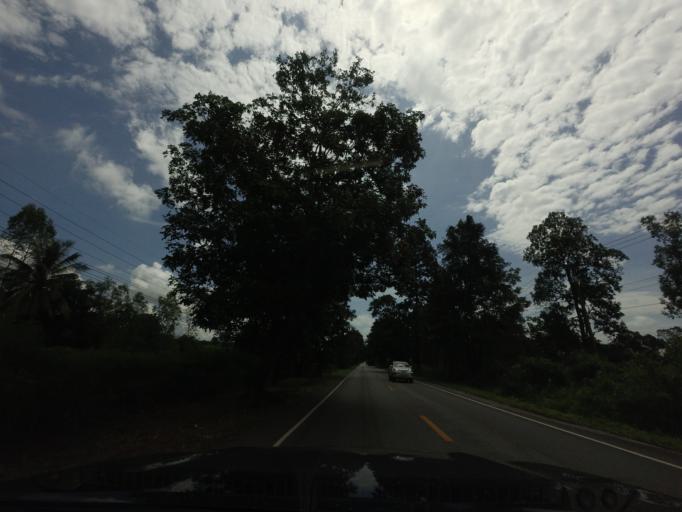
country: TH
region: Nong Khai
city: Pho Tak
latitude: 17.8054
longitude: 102.3413
